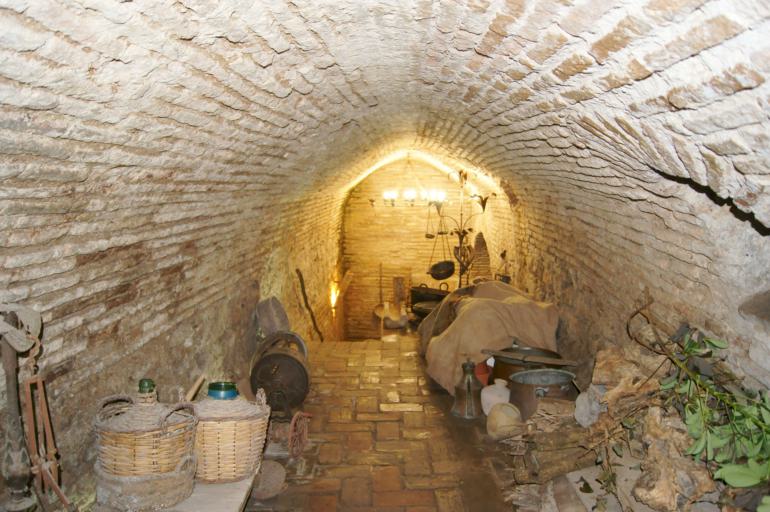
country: ES
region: Andalusia
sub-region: Province of Cordoba
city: Cordoba
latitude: 37.8802
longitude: -4.7836
